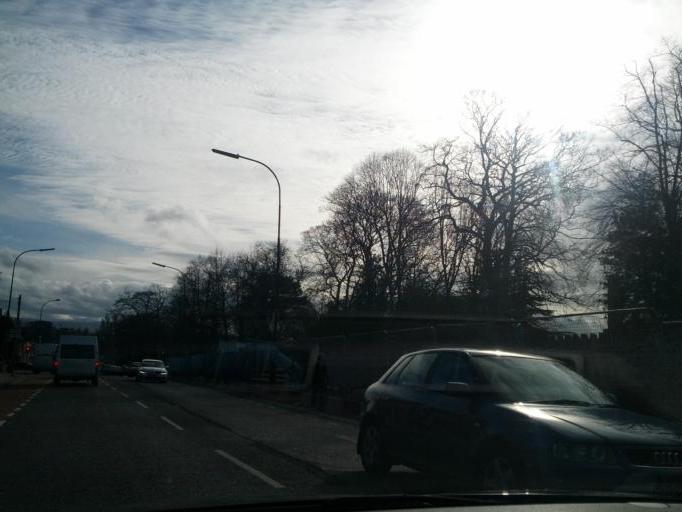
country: IE
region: Leinster
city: Drumcondra
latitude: 53.3716
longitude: -6.2532
